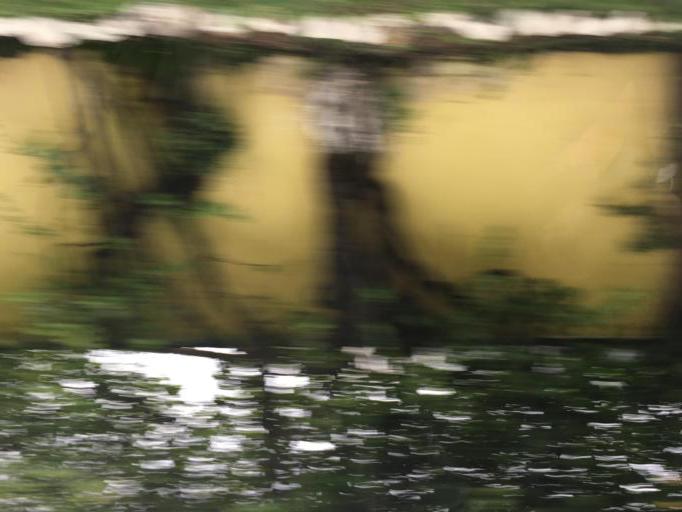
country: GT
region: Guatemala
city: Villa Canales
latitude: 14.4225
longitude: -90.5465
